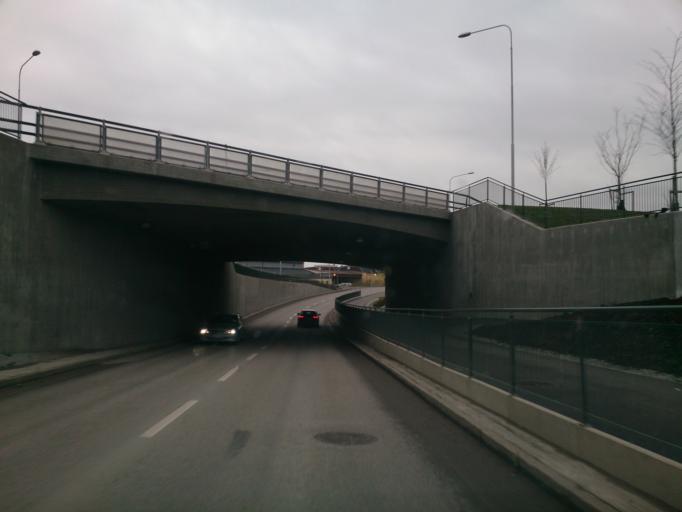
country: SE
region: OEstergoetland
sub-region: Linkopings Kommun
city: Linkoping
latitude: 58.4024
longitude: 15.6500
